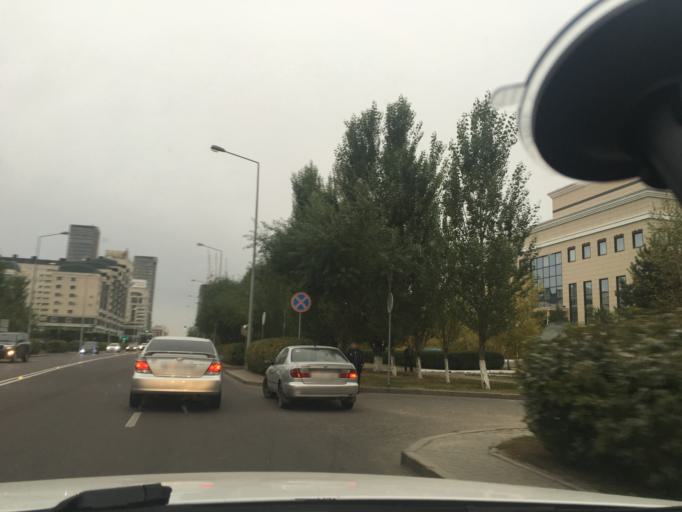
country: KZ
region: Astana Qalasy
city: Astana
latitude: 51.1321
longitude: 71.4339
